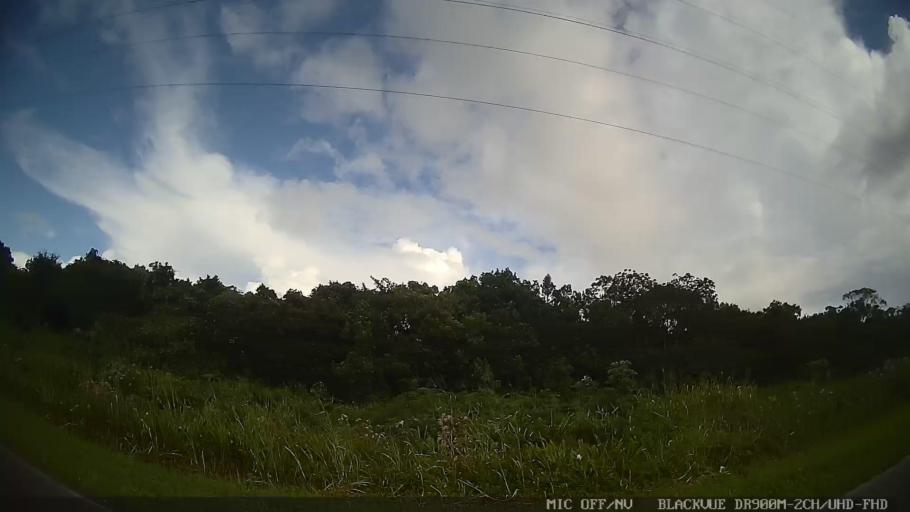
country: BR
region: Sao Paulo
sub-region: Peruibe
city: Peruibe
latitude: -24.2442
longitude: -46.9182
